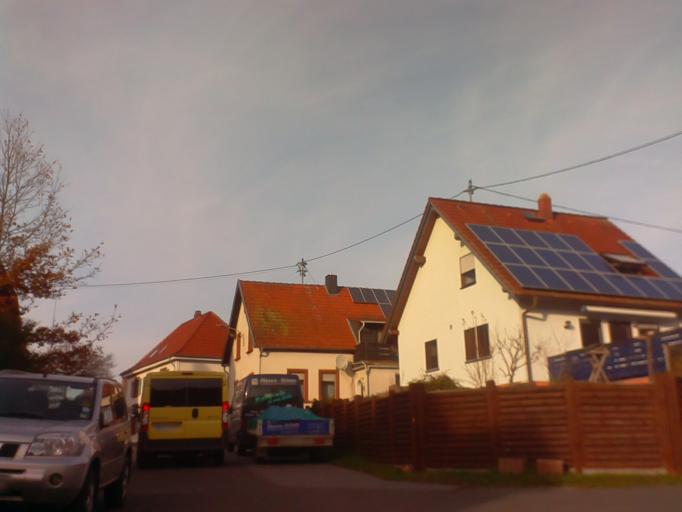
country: DE
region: Rheinland-Pfalz
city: Carlsberg
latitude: 49.4912
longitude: 8.0307
